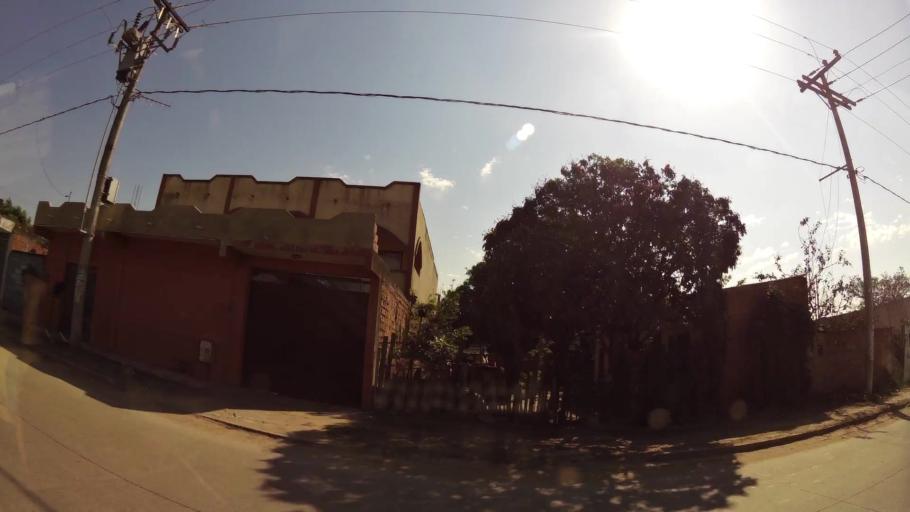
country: BO
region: Santa Cruz
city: Cotoca
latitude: -17.7999
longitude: -63.1091
